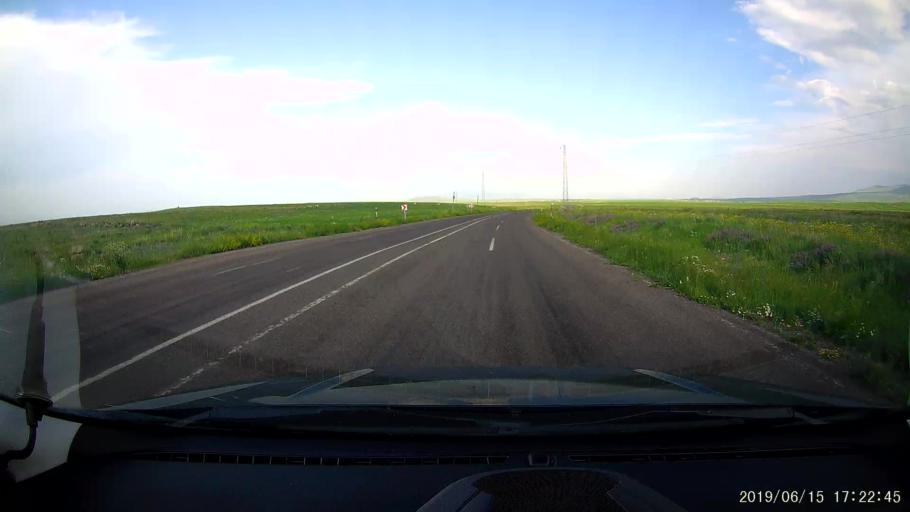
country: TR
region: Kars
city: Basgedikler
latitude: 40.6193
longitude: 43.3491
